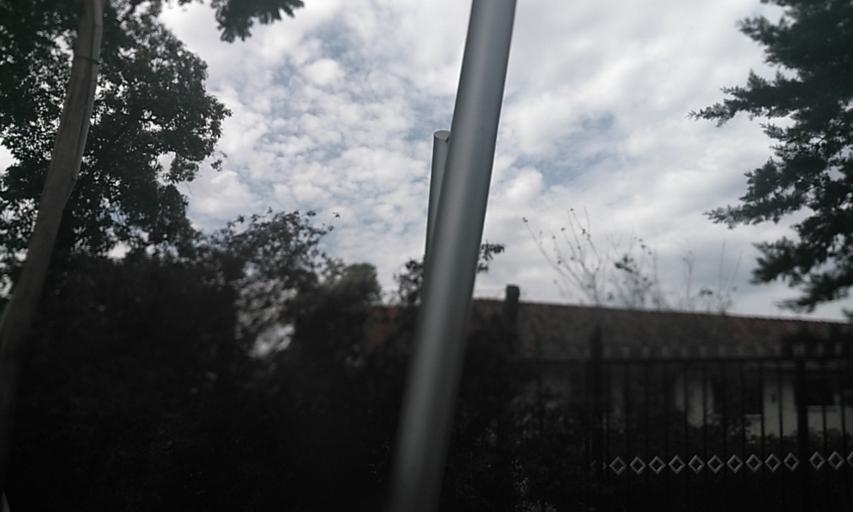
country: UG
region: Central Region
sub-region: Kampala District
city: Kampala
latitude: 0.3224
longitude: 32.5946
